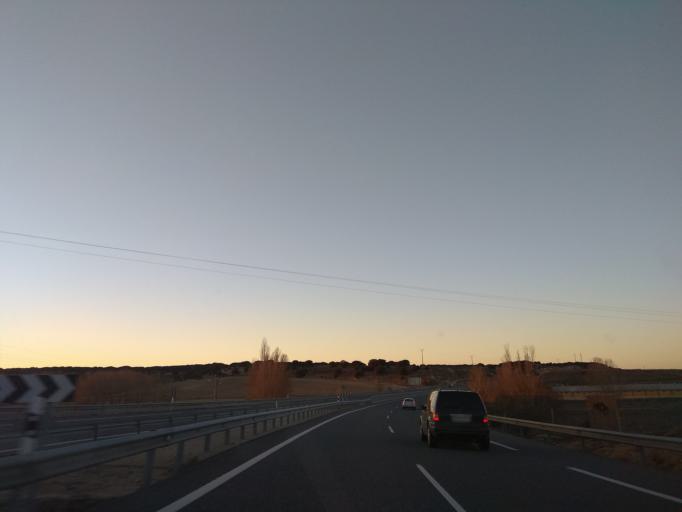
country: ES
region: Castille and Leon
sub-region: Provincia de Burgos
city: Bahabon de Esgueva
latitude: 41.8994
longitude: -3.7479
